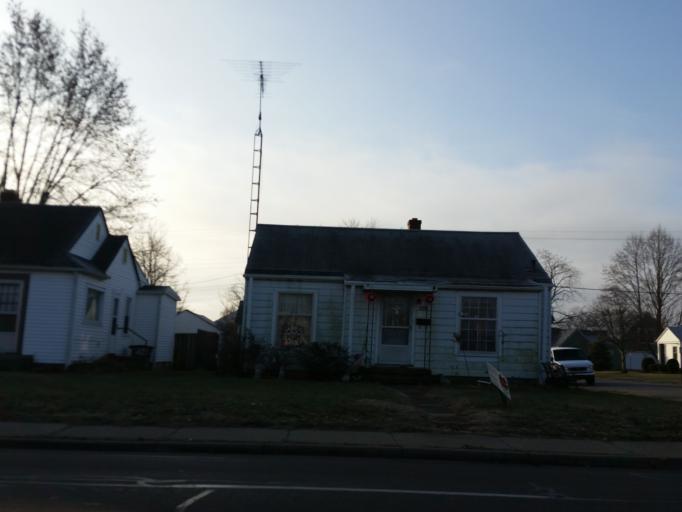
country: US
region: Indiana
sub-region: Bartholomew County
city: Columbus
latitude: 39.2230
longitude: -85.9119
